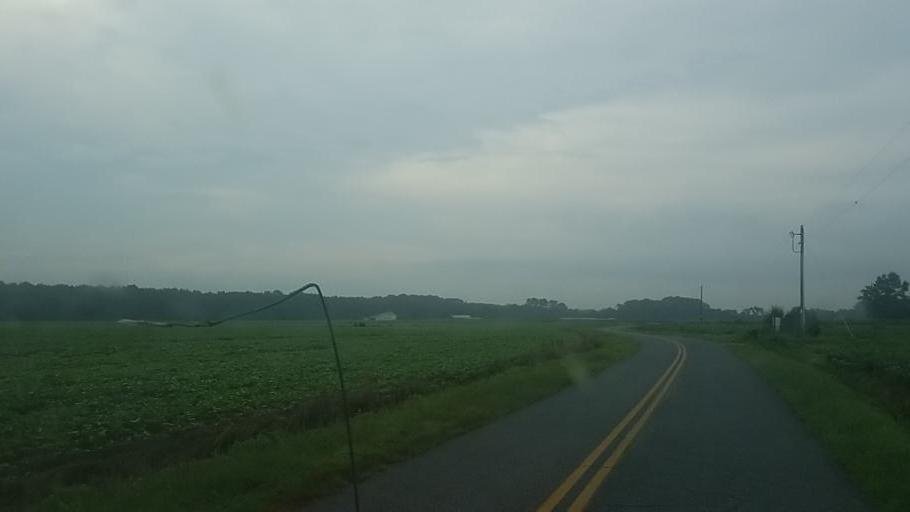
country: US
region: Maryland
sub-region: Wicomico County
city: Pittsville
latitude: 38.4249
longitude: -75.3202
